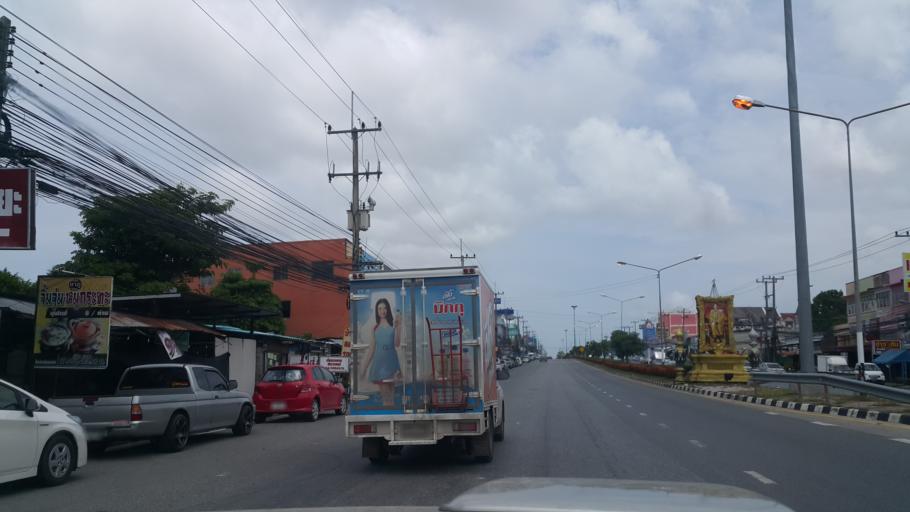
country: TH
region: Rayong
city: Ban Chang
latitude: 12.7221
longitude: 101.0501
